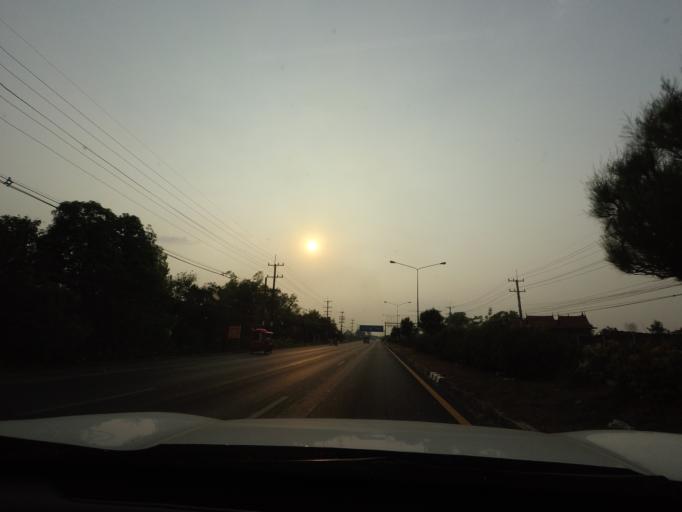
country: TH
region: Nakhon Nayok
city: Pak Phli
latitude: 14.1484
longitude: 101.2904
